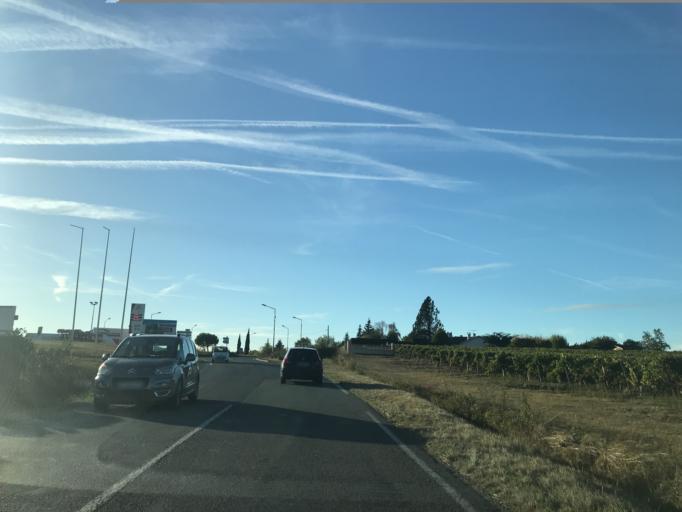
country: FR
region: Poitou-Charentes
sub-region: Departement de la Charente-Maritime
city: Montguyon
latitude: 45.2119
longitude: -0.1746
